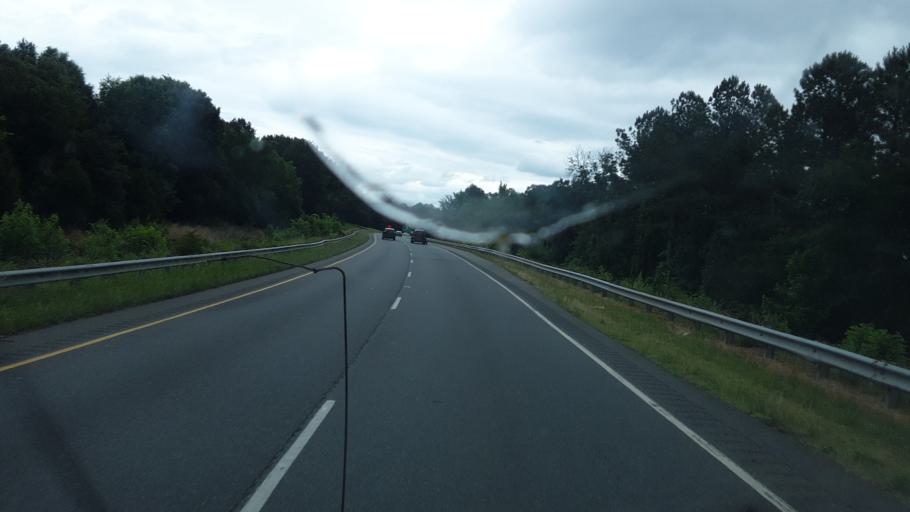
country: US
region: North Carolina
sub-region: Forsyth County
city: Clemmons
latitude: 36.0696
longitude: -80.3251
